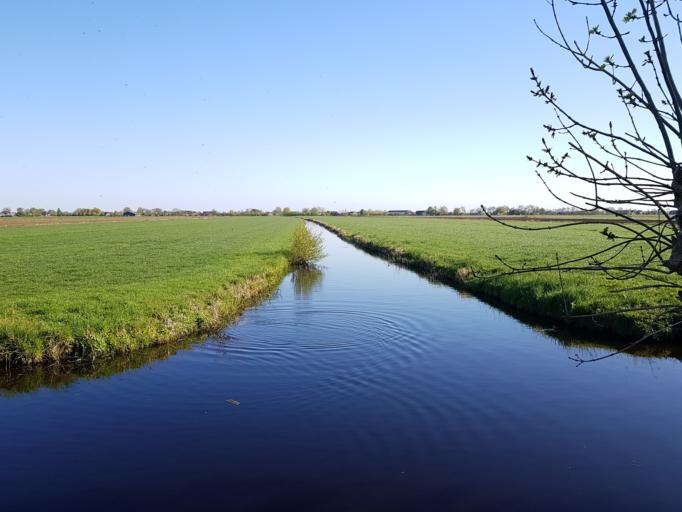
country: NL
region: South Holland
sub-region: Gemeente Vlist
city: Vlist
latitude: 52.0116
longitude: 4.8317
